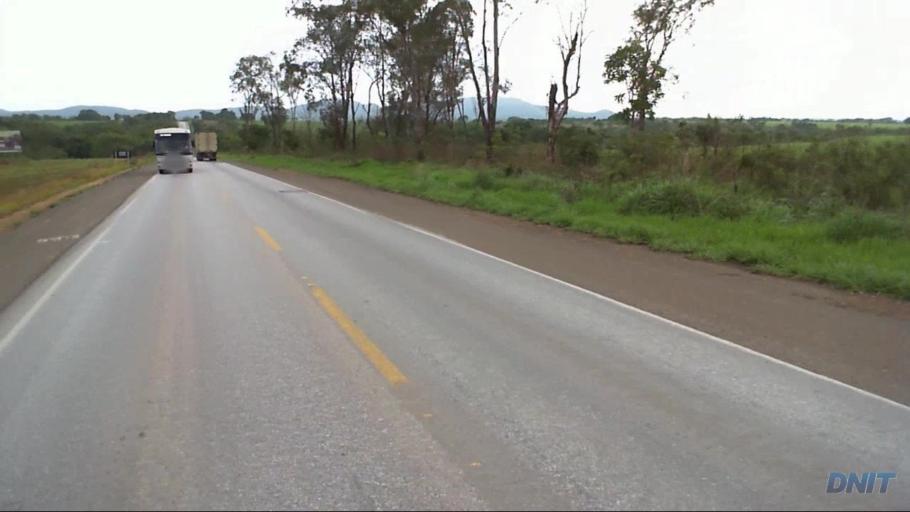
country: BR
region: Goias
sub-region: Uruacu
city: Uruacu
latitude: -14.6177
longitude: -49.1703
